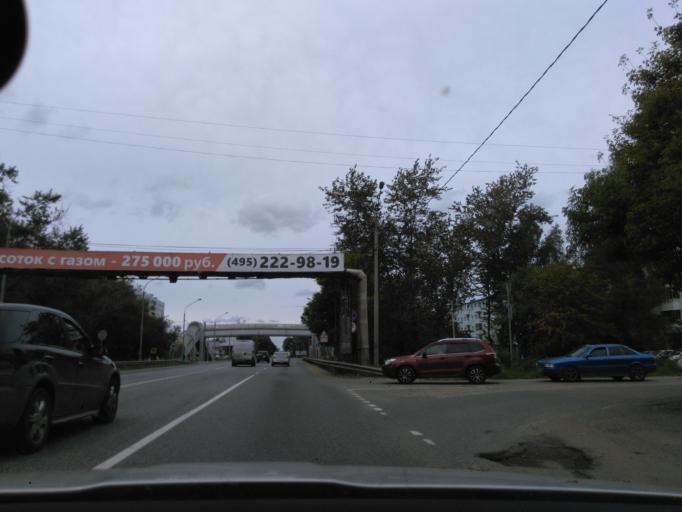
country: RU
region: Moskovskaya
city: Klin
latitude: 56.3236
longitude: 36.7575
